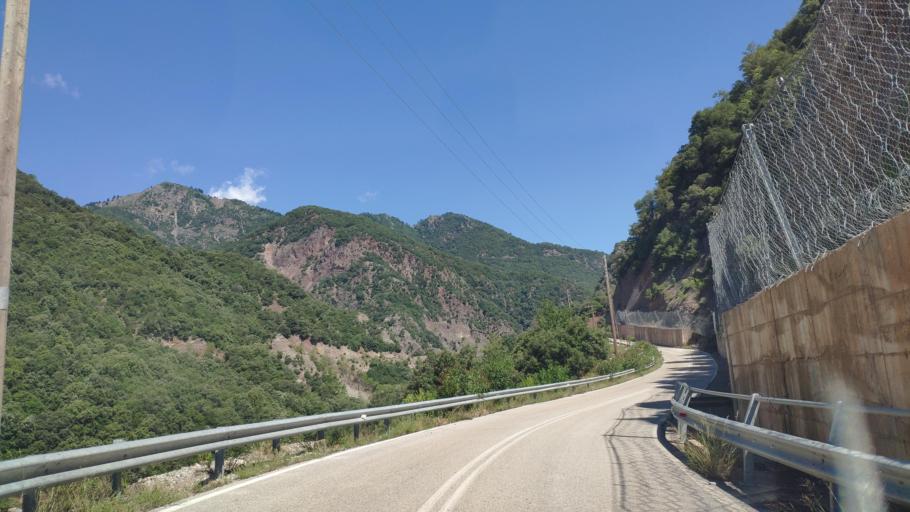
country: GR
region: Central Greece
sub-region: Nomos Evrytanias
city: Kerasochori
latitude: 39.0394
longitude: 21.5958
